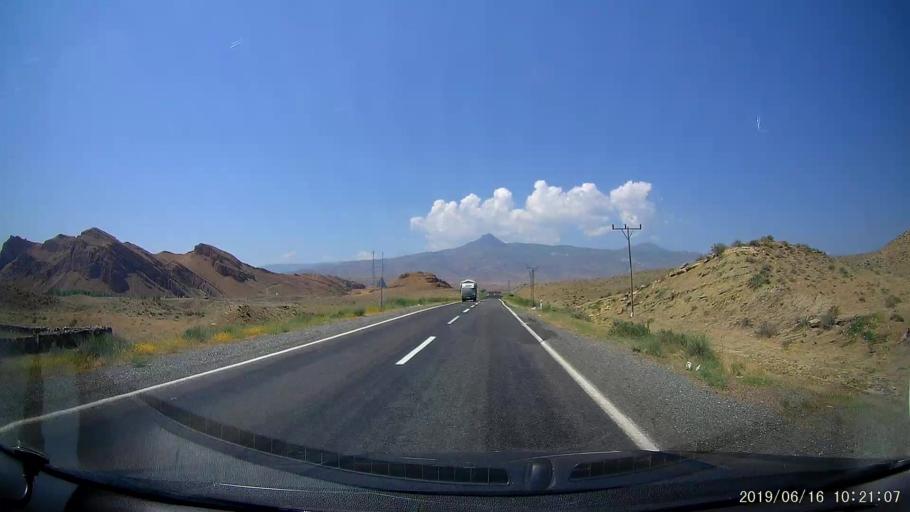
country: TR
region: Igdir
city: Tuzluca
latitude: 40.1407
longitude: 43.6401
